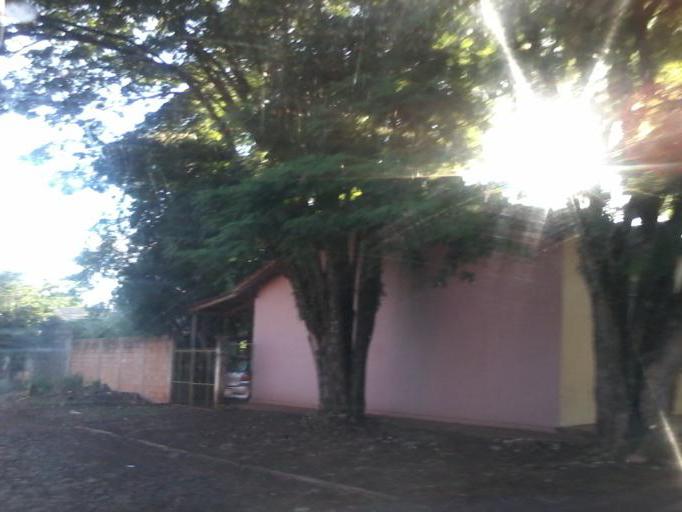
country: PY
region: Alto Parana
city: Ciudad del Este
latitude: -25.4370
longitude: -54.6407
